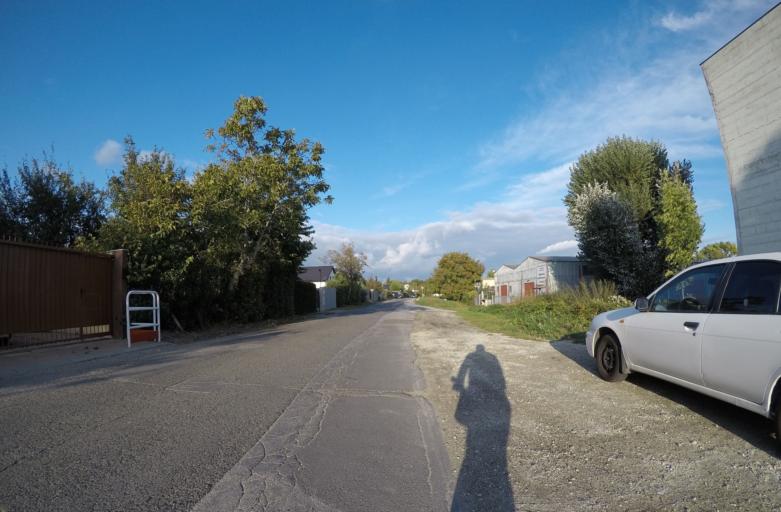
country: SK
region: Bratislavsky
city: Bratislava
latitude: 48.1775
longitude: 17.1751
